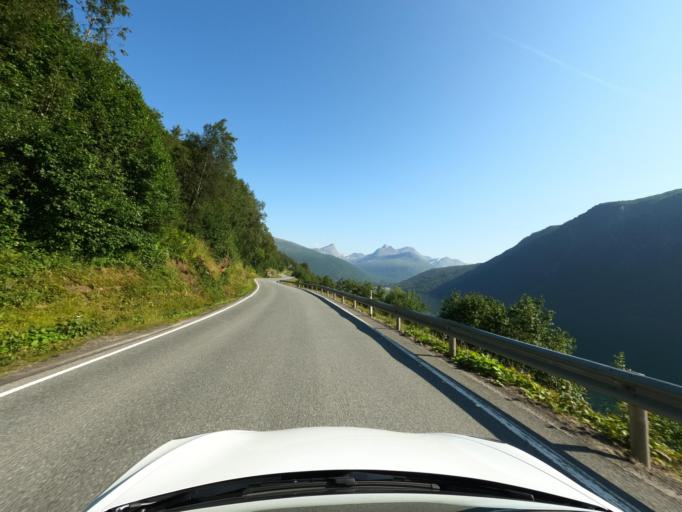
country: NO
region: Nordland
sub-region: Narvik
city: Narvik
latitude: 68.3931
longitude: 17.5324
